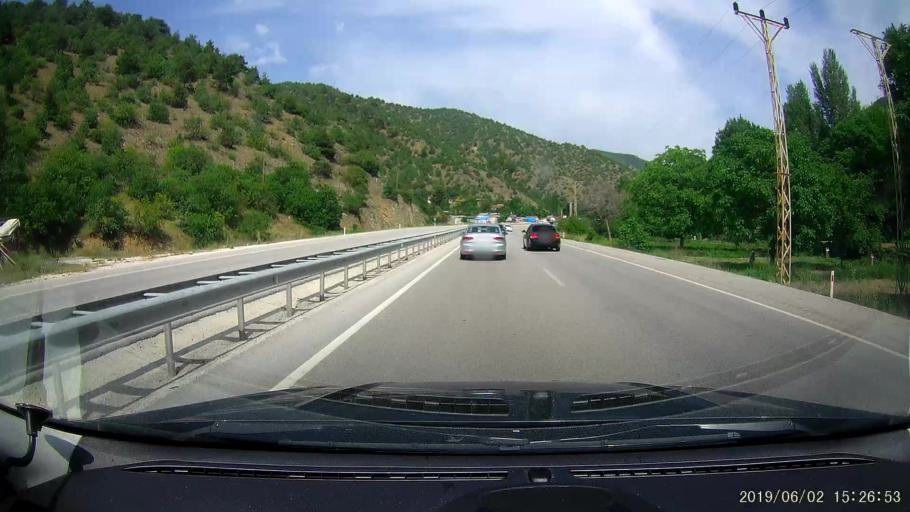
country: TR
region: Amasya
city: Saraycik
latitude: 40.9869
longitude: 35.0462
